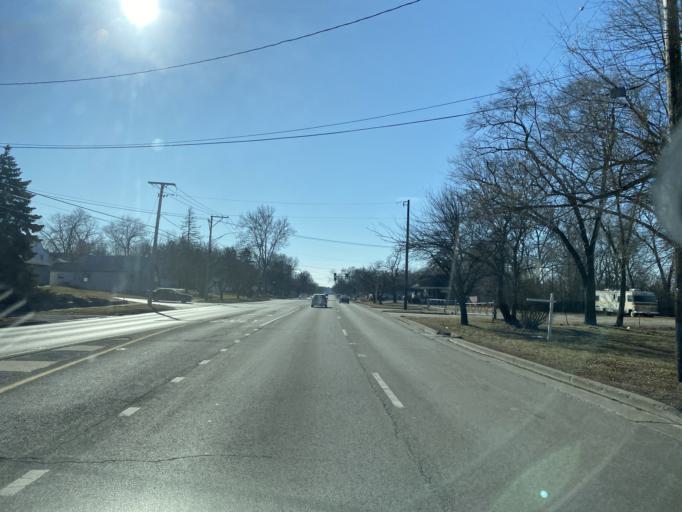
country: US
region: Illinois
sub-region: Will County
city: Lockport
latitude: 41.5978
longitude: -88.0536
